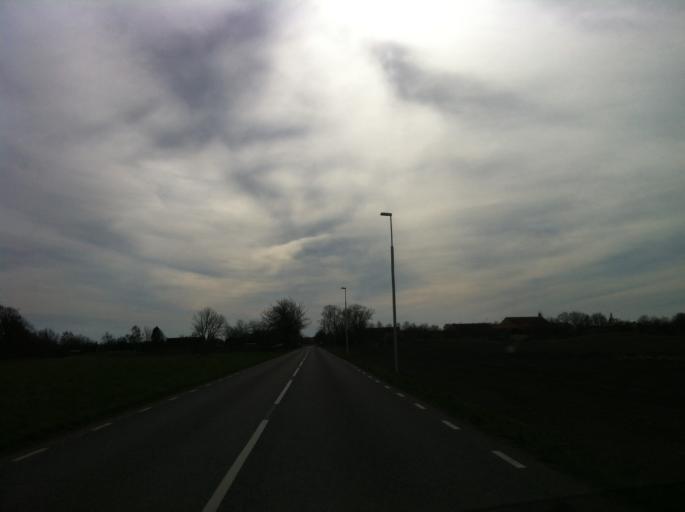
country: SE
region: Skane
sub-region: Hoganas Kommun
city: Hoganas
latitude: 56.2457
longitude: 12.5468
